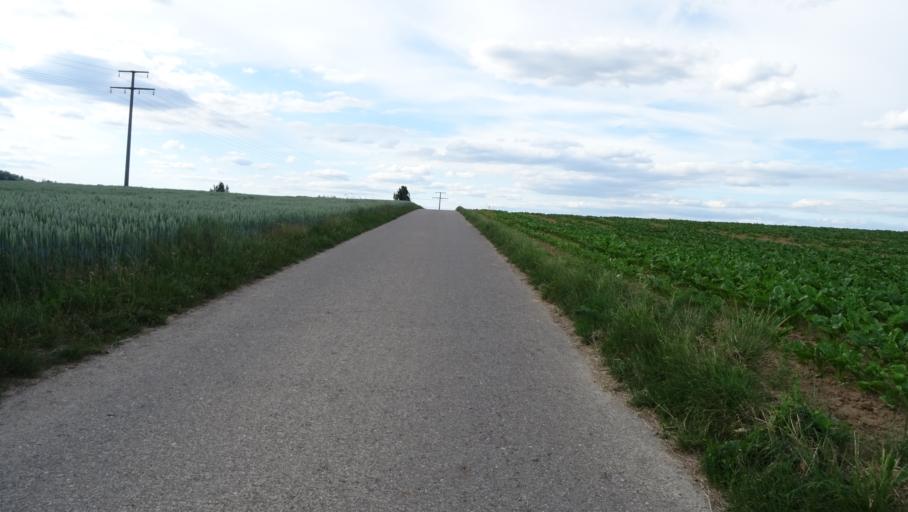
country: DE
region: Baden-Wuerttemberg
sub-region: Regierungsbezirk Stuttgart
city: Offenau
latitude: 49.2618
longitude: 9.1662
